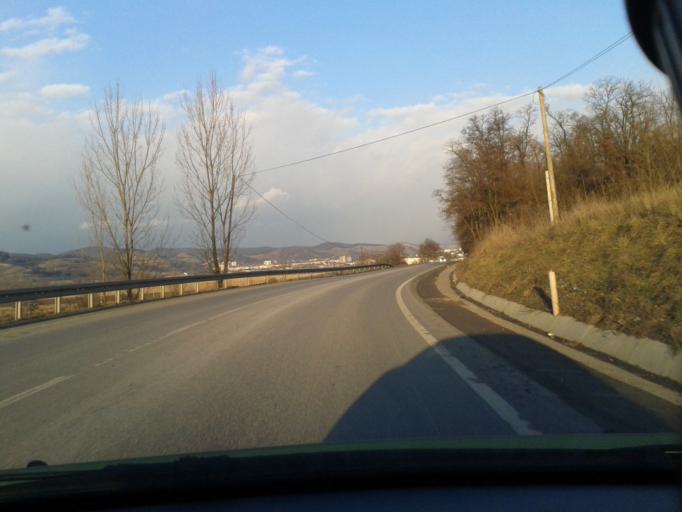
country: RO
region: Sibiu
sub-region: Comuna Tarnava
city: Tarnava
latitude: 46.1387
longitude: 24.3115
